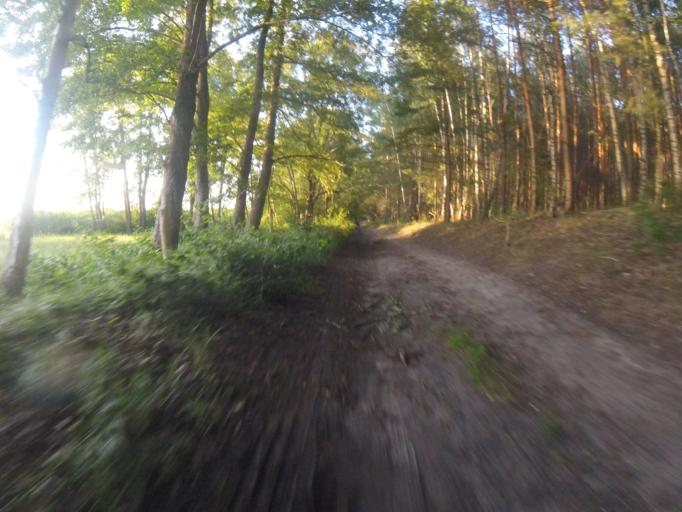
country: DE
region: Brandenburg
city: Gross Koris
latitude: 52.1761
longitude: 13.7001
